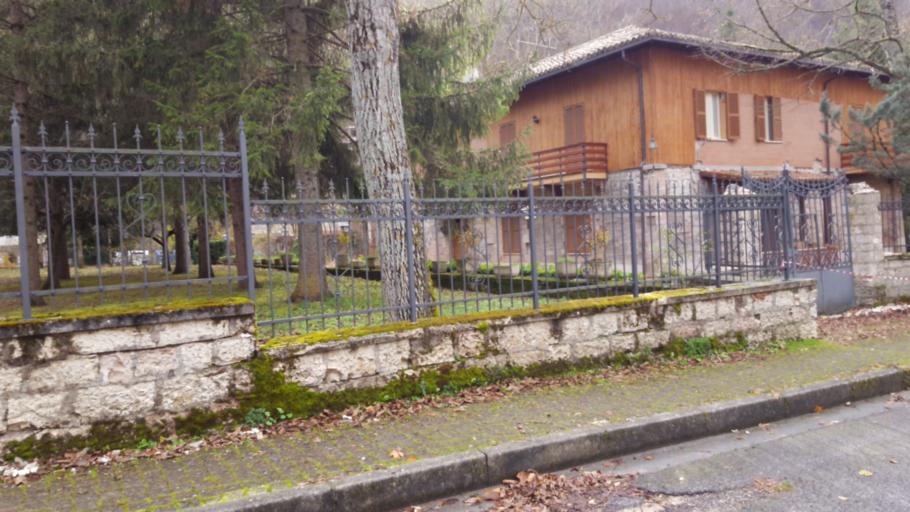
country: IT
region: The Marches
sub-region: Provincia di Macerata
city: Pieve
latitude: 42.9432
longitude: 13.1378
